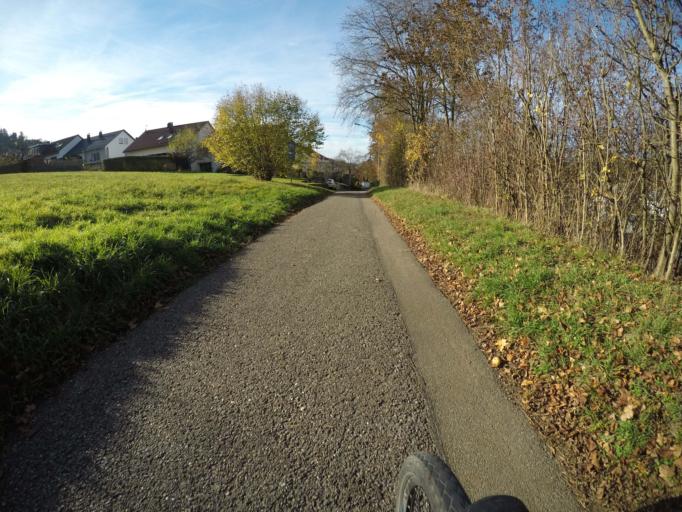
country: DE
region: Baden-Wuerttemberg
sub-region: Regierungsbezirk Stuttgart
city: Winterbach
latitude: 48.8097
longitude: 9.4233
